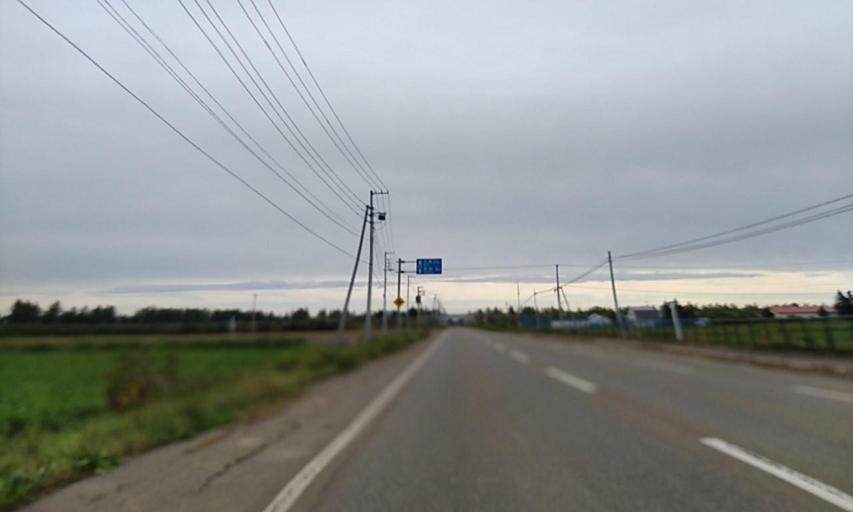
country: JP
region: Hokkaido
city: Obihiro
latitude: 42.6834
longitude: 143.1435
